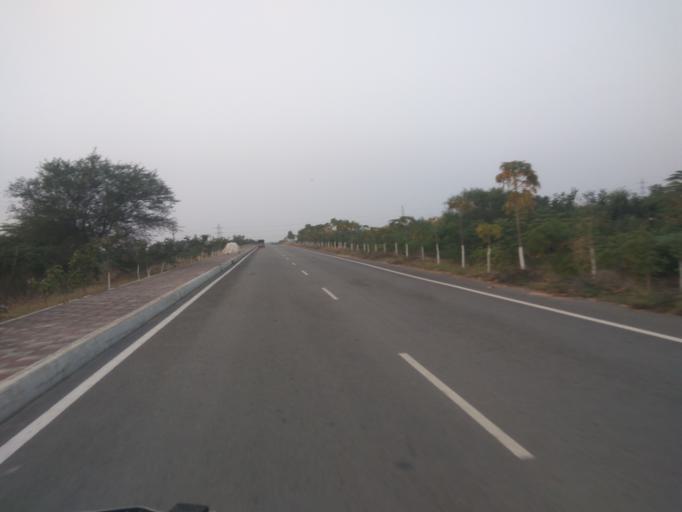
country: IN
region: Telangana
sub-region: Rangareddi
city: Secunderabad
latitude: 17.5439
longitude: 78.6304
